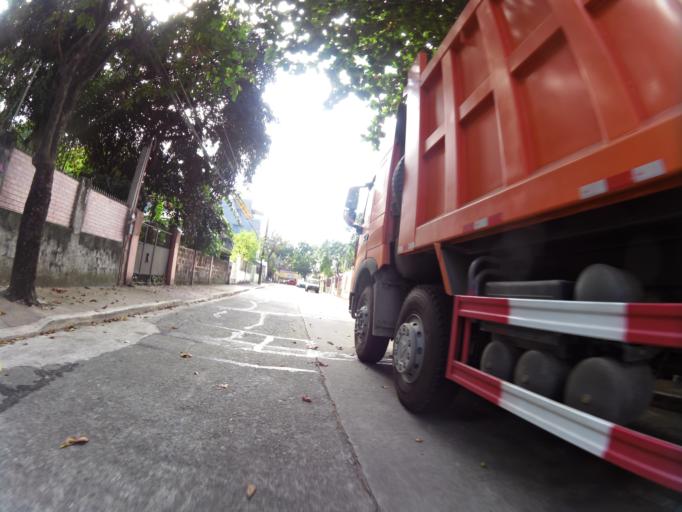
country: PH
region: Metro Manila
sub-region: Marikina
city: Calumpang
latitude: 14.6262
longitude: 121.1002
